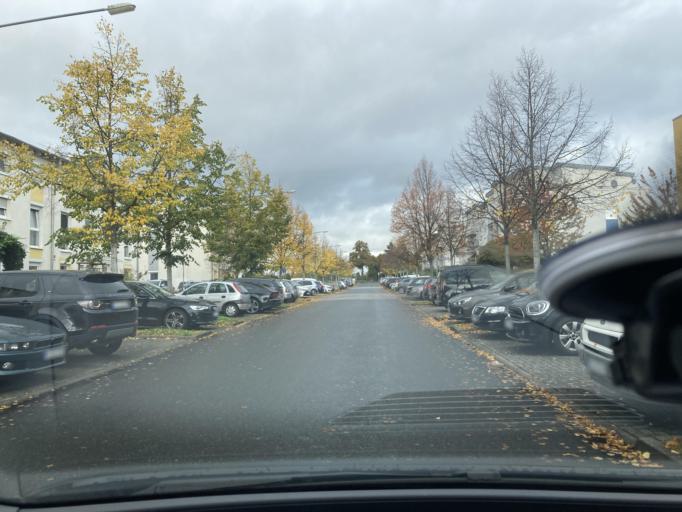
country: DE
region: Hesse
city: Sulzbach
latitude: 50.1133
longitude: 8.5515
